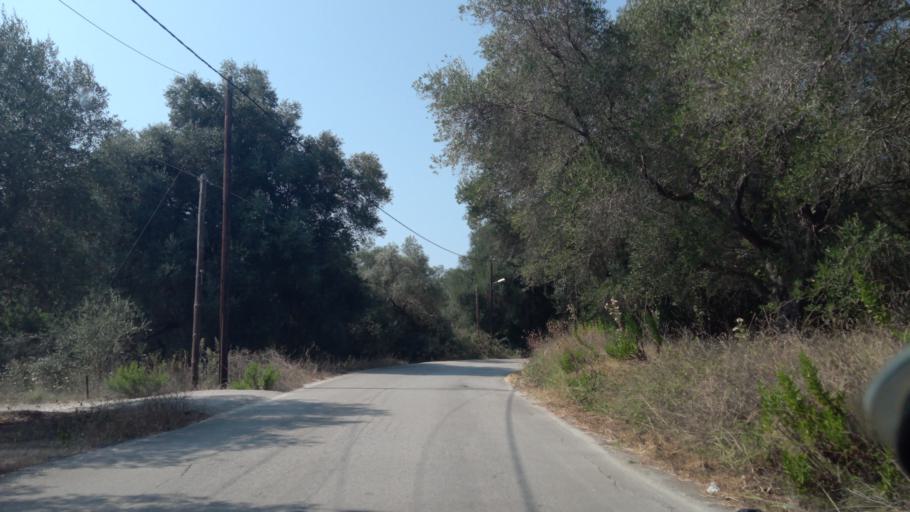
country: GR
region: Ionian Islands
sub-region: Nomos Kerkyras
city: Perivoli
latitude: 39.4134
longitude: 20.0281
